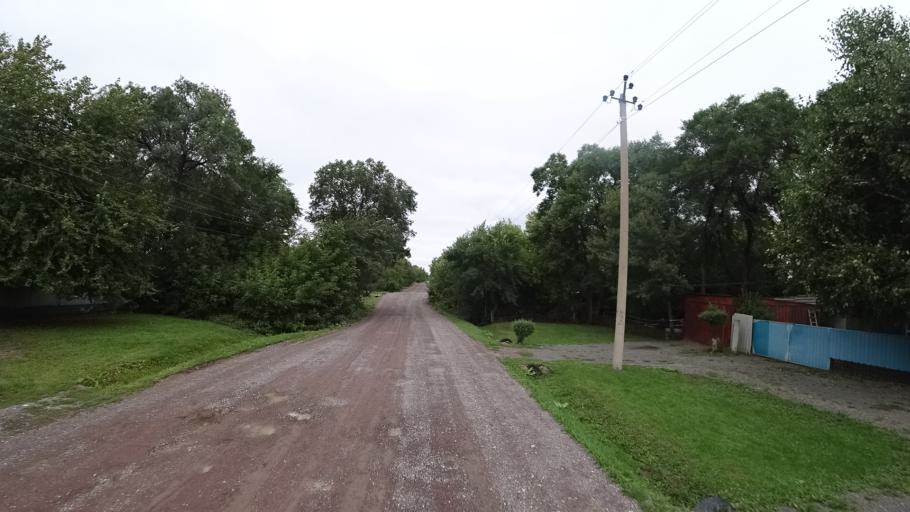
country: RU
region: Primorskiy
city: Chernigovka
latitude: 44.3389
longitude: 132.5907
